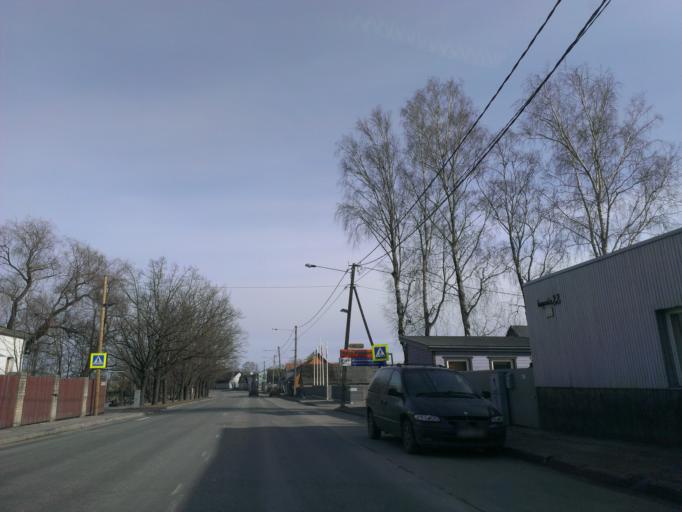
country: EE
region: Paernumaa
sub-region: Paernu linn
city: Parnu
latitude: 58.3885
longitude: 24.4766
